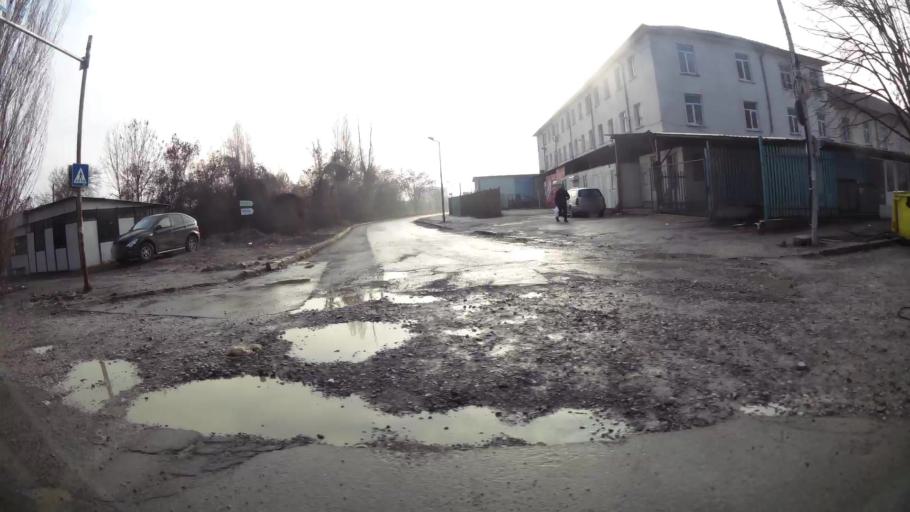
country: BG
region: Sofia-Capital
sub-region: Stolichna Obshtina
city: Sofia
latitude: 42.7293
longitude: 23.3193
